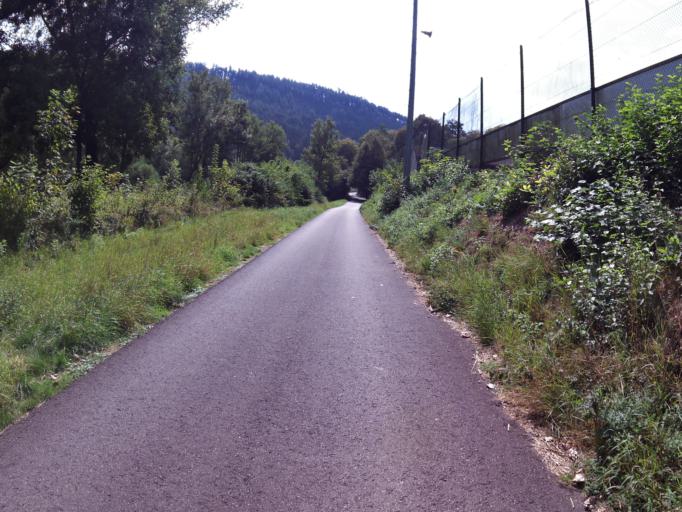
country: DE
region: Rheinland-Pfalz
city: Kordel
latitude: 49.8455
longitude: 6.6407
